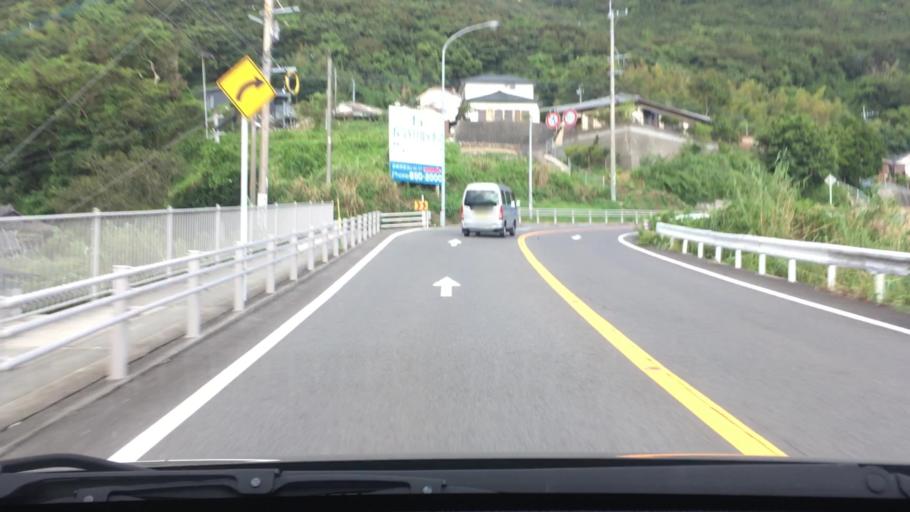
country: JP
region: Nagasaki
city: Togitsu
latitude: 32.8308
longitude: 129.7219
